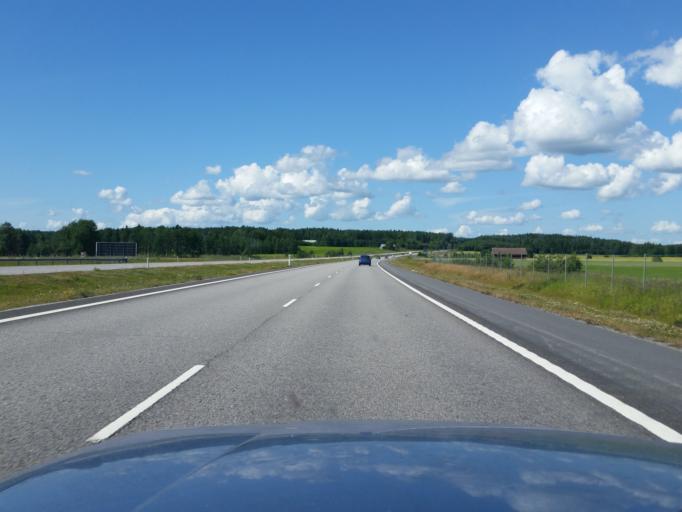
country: FI
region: Varsinais-Suomi
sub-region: Salo
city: Halikko
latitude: 60.4176
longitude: 23.1075
